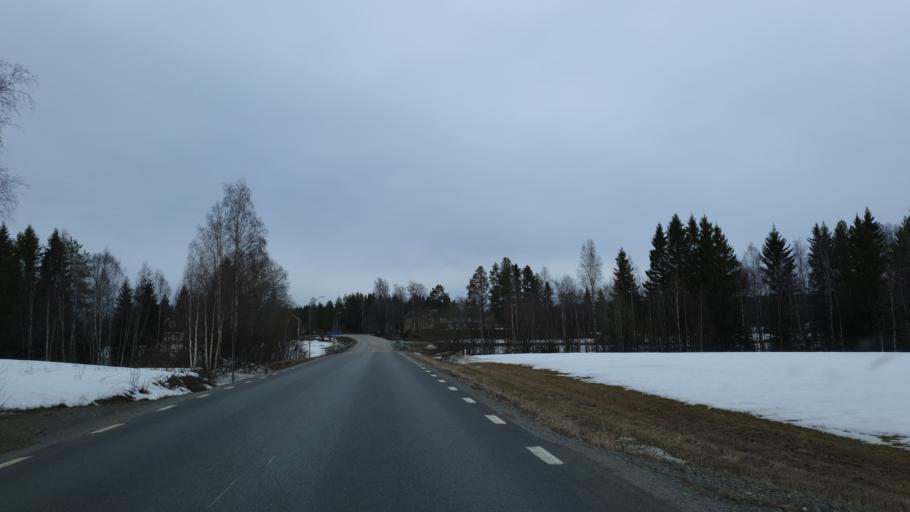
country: SE
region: Vaesterbotten
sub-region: Robertsfors Kommun
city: Robertsfors
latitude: 64.3897
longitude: 20.8961
